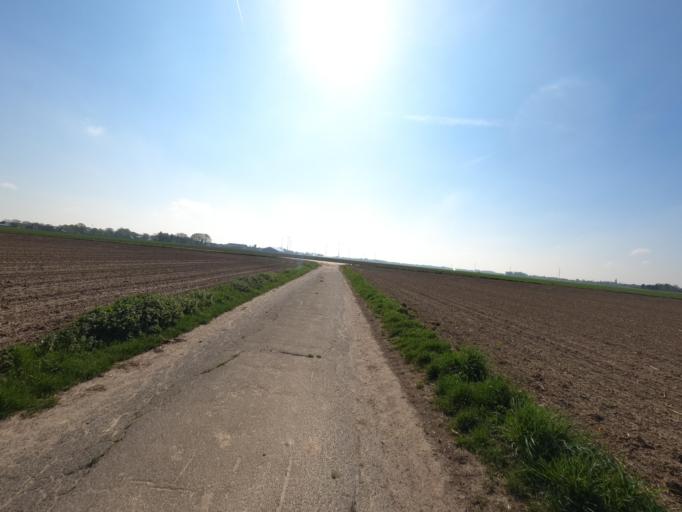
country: DE
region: North Rhine-Westphalia
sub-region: Regierungsbezirk Koln
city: Heinsberg
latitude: 51.0323
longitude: 6.0652
